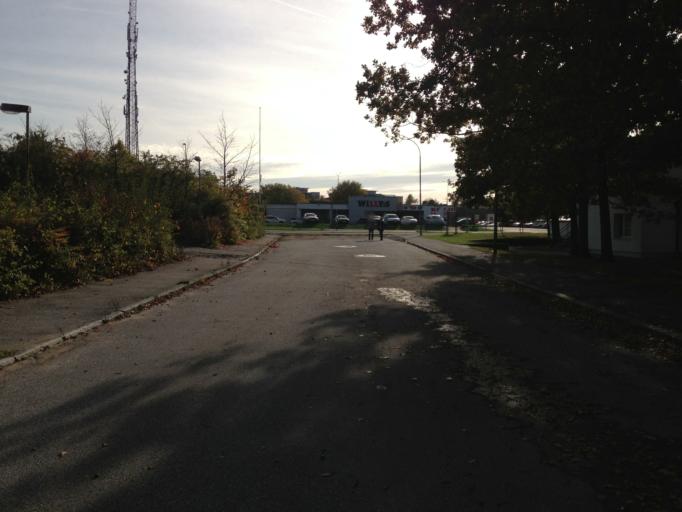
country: SE
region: Skane
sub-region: Lunds Kommun
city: Lund
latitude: 55.7212
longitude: 13.2217
